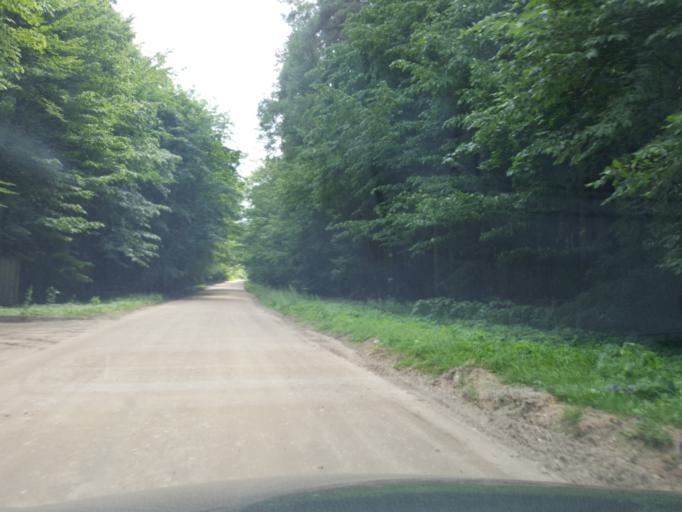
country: LT
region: Alytaus apskritis
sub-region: Alytus
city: Alytus
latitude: 54.3812
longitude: 24.0421
